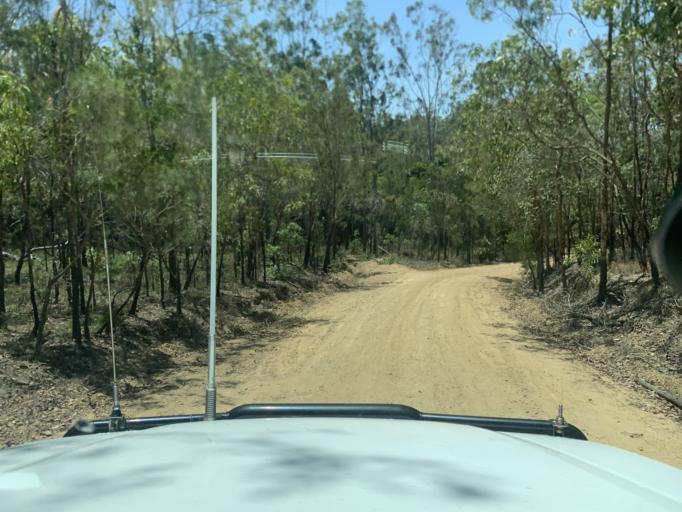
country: AU
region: Queensland
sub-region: Cairns
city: Redlynch
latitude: -16.9355
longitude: 145.6011
